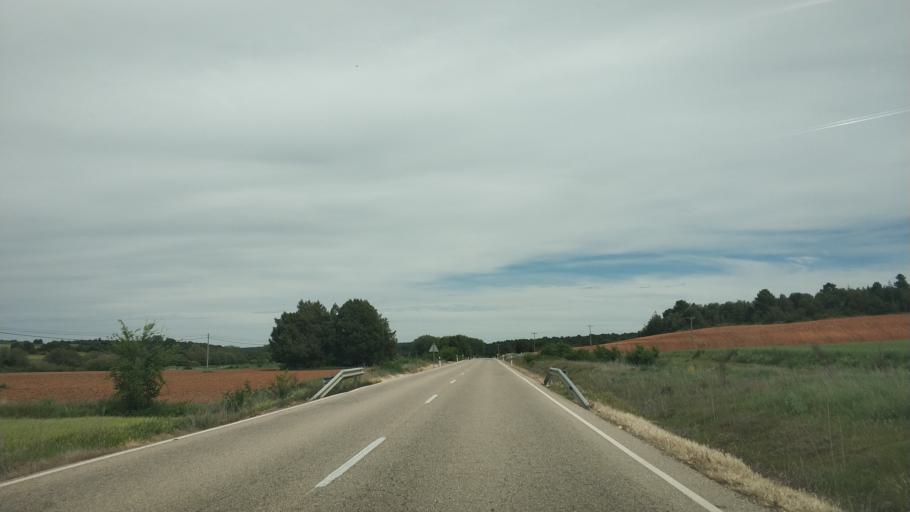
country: ES
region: Castille and Leon
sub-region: Provincia de Soria
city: Valdenebro
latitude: 41.5684
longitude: -3.0051
